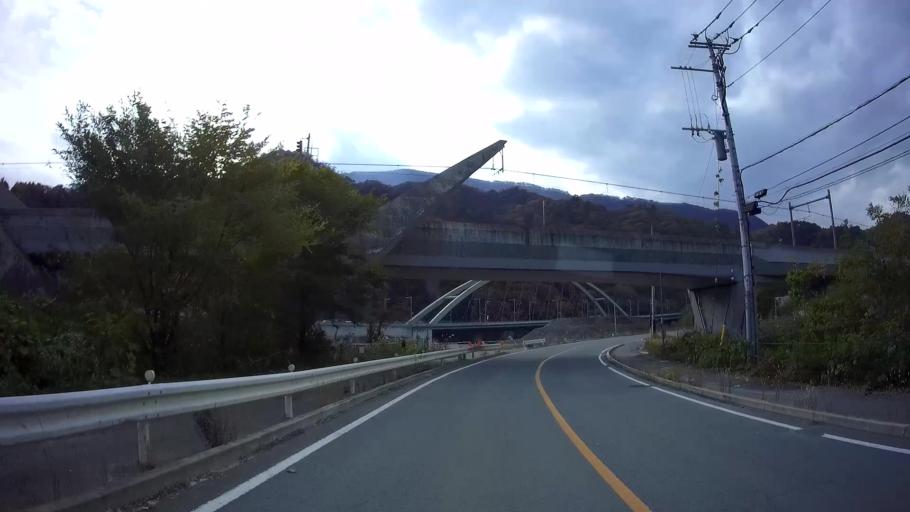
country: JP
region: Gunma
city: Nakanojomachi
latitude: 36.5452
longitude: 138.6550
